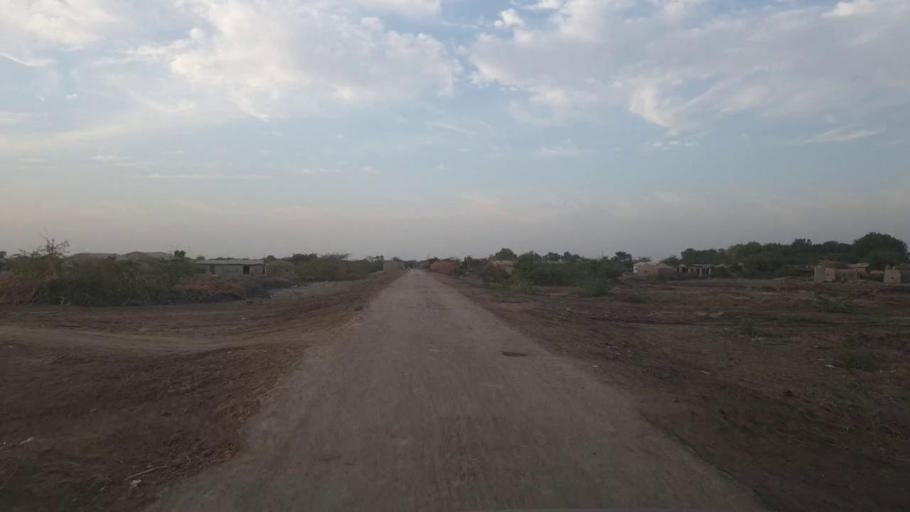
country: PK
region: Sindh
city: Umarkot
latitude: 25.2777
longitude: 69.6847
